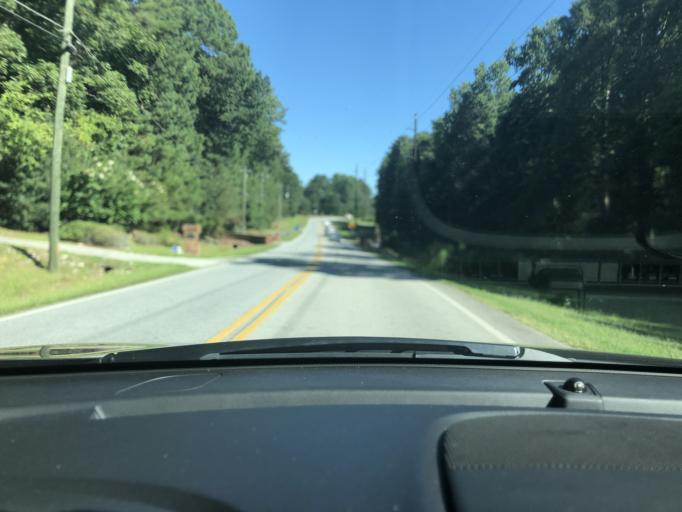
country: US
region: Georgia
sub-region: Gwinnett County
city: Grayson
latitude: 33.9238
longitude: -83.9499
